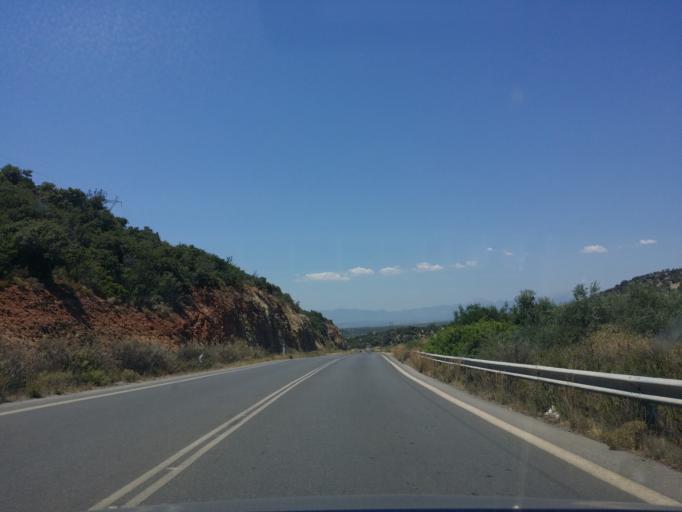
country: GR
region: Peloponnese
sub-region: Nomos Lakonias
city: Kato Glikovrisi
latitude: 36.8607
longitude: 22.7966
